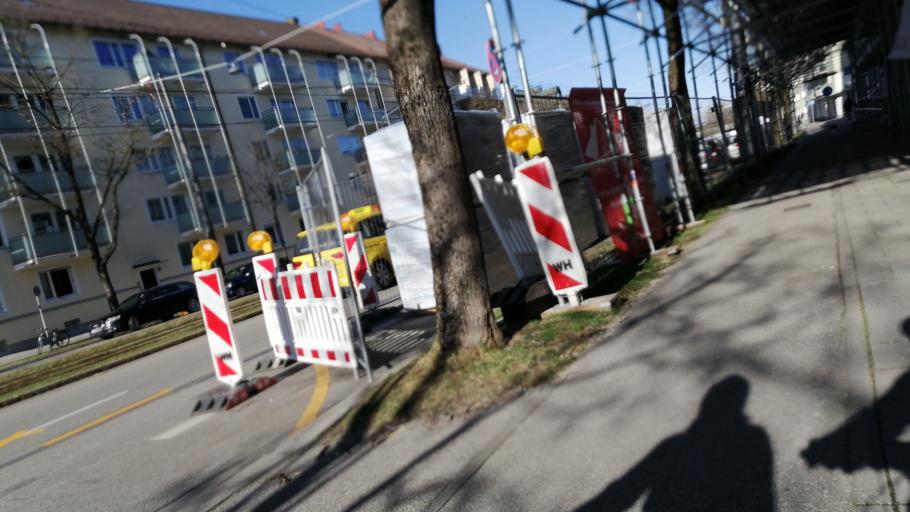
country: DE
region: Bavaria
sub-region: Upper Bavaria
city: Pasing
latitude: 48.1284
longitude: 11.5150
